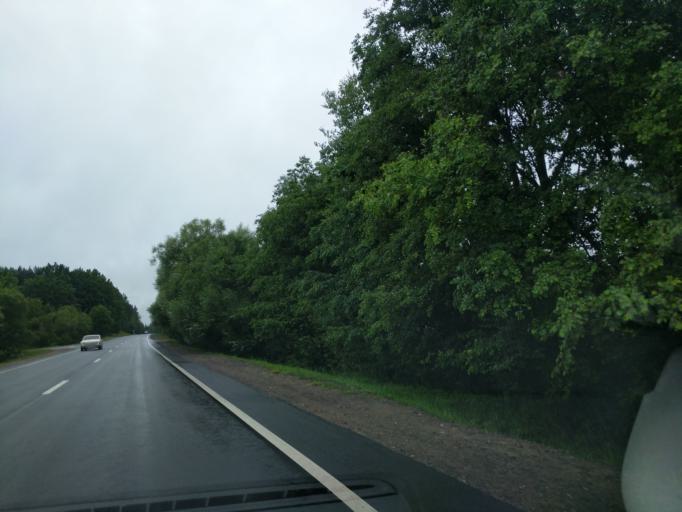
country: BY
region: Minsk
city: Syomkava
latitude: 54.1885
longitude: 27.4998
